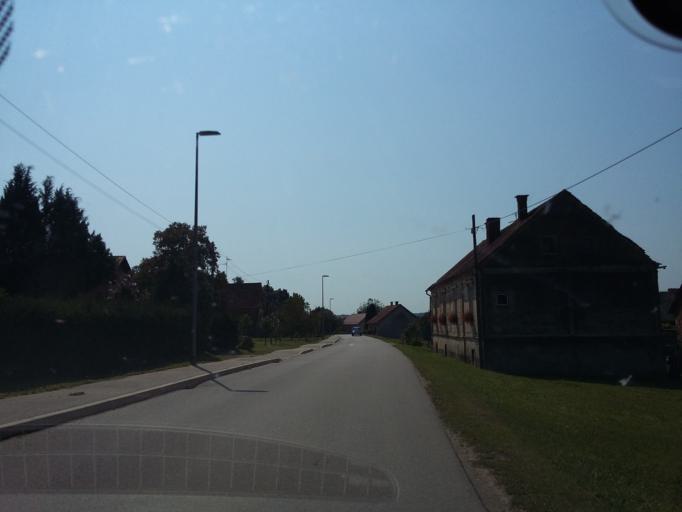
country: SI
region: Hodos-Hodos
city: Hodos
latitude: 46.8319
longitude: 16.3206
